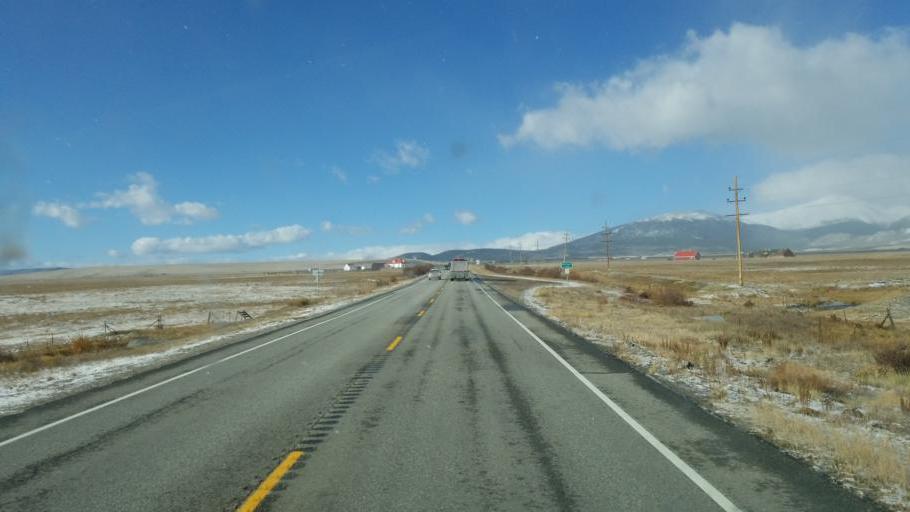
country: US
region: Colorado
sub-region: Park County
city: Fairplay
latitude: 39.3510
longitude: -105.8313
